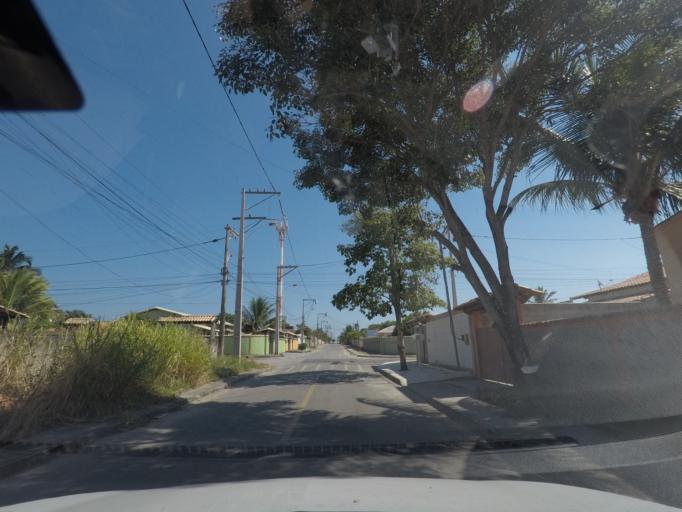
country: BR
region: Rio de Janeiro
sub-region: Niteroi
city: Niteroi
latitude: -22.9619
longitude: -42.9720
